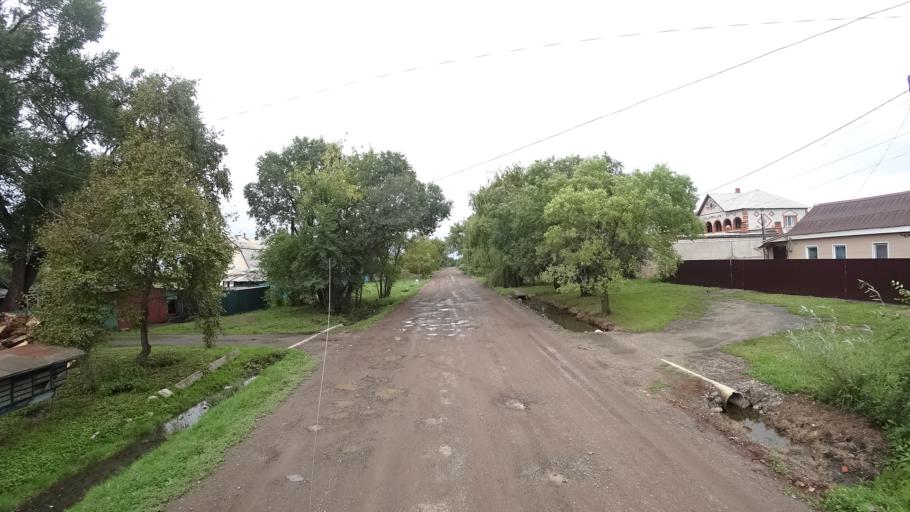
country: RU
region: Primorskiy
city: Chernigovka
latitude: 44.3353
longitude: 132.5661
